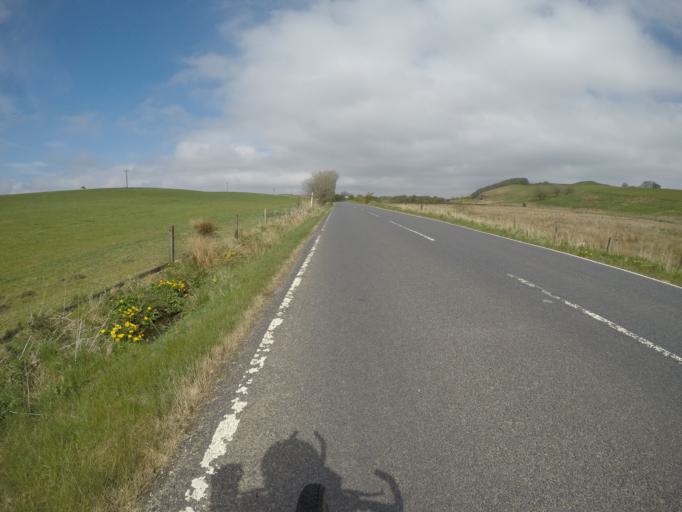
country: GB
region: Scotland
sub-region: East Renfrewshire
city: Neilston
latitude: 55.7271
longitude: -4.4223
